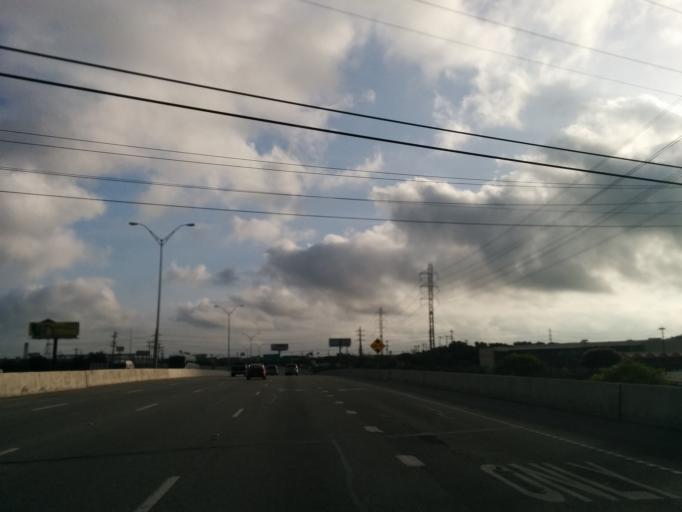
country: US
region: Texas
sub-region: Bexar County
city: Alamo Heights
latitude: 29.5075
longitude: -98.4779
